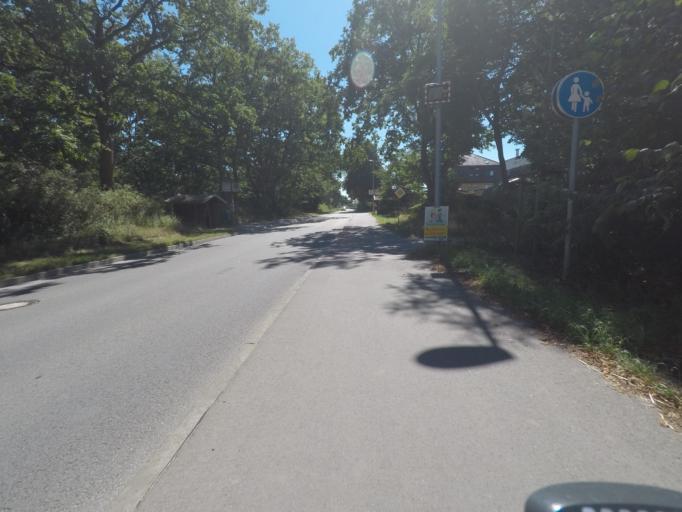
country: DE
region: Schleswig-Holstein
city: Trittau
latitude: 53.6256
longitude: 10.4021
